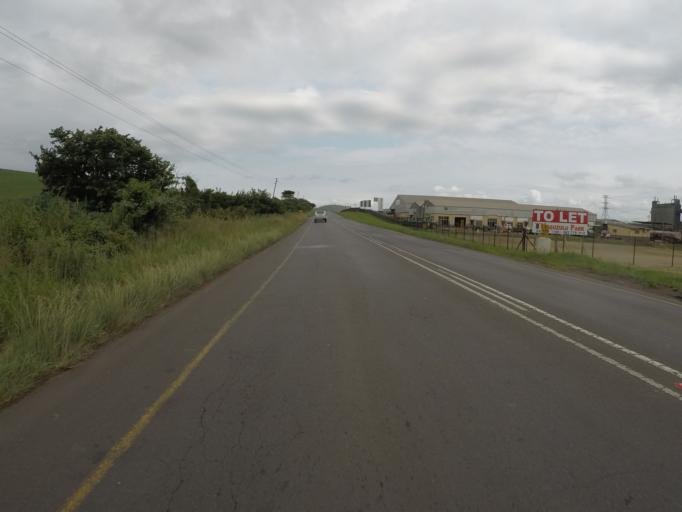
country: ZA
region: KwaZulu-Natal
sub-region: uThungulu District Municipality
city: Empangeni
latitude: -28.7284
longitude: 31.8700
